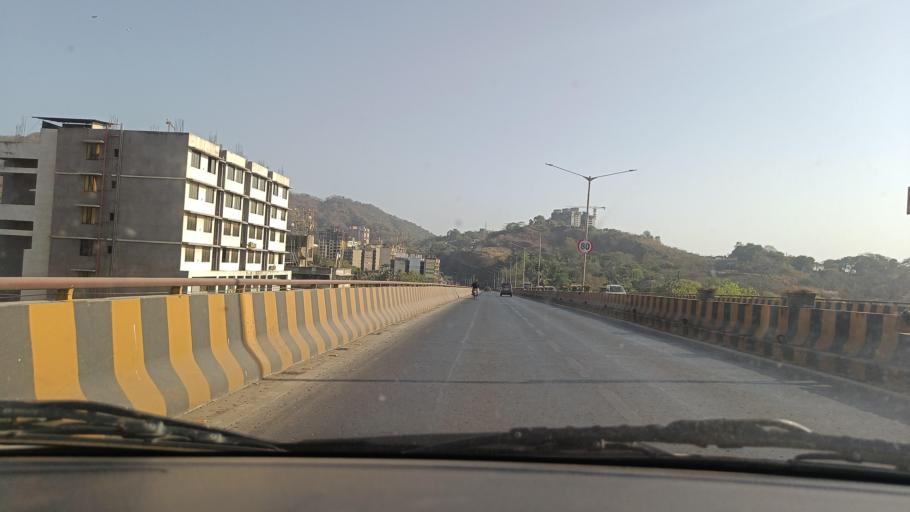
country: IN
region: Maharashtra
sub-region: Mumbai Suburban
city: Mumbai
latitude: 19.0453
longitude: 72.9091
